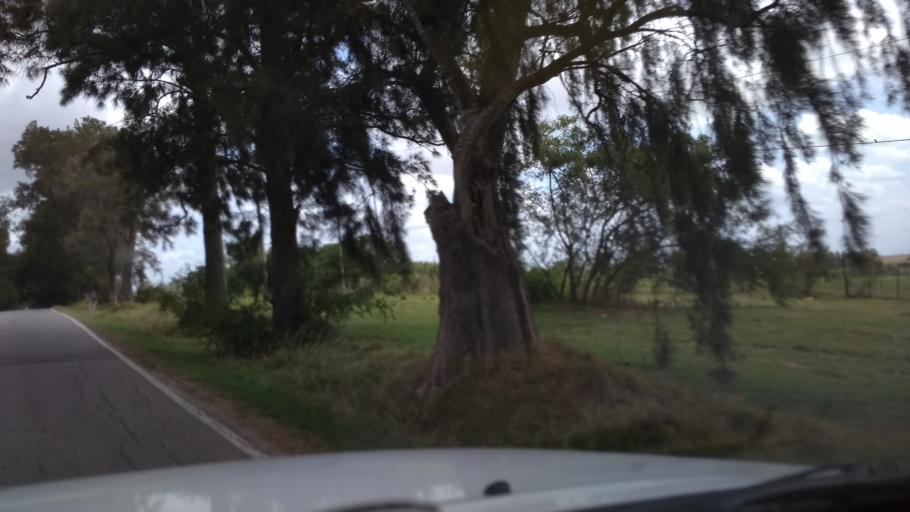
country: UY
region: Canelones
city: San Ramon
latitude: -34.3584
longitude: -55.9595
